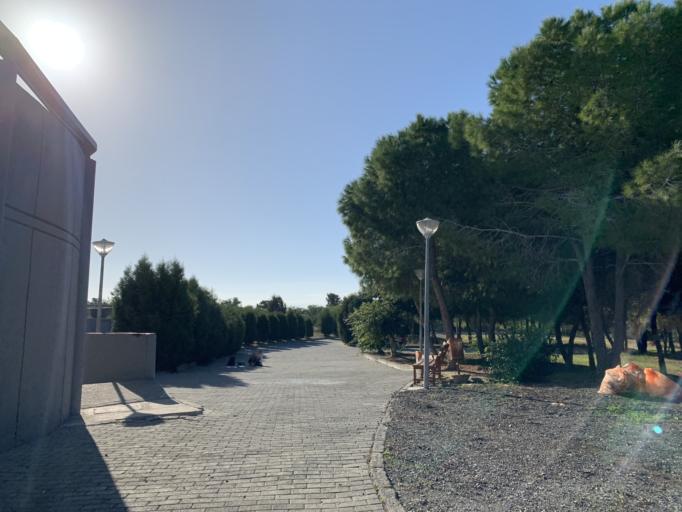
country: CY
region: Larnaka
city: Larnaca
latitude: 34.9061
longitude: 33.6251
